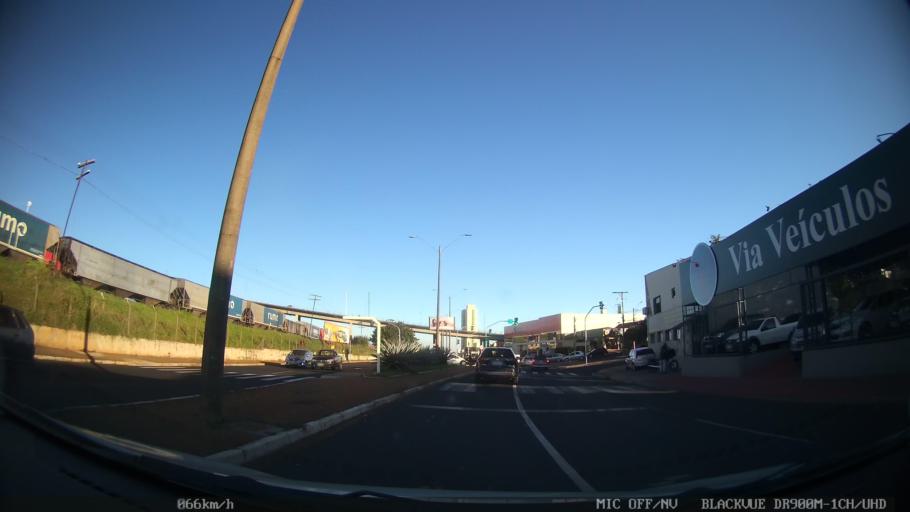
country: BR
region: Sao Paulo
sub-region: Araraquara
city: Araraquara
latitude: -21.7862
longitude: -48.1723
